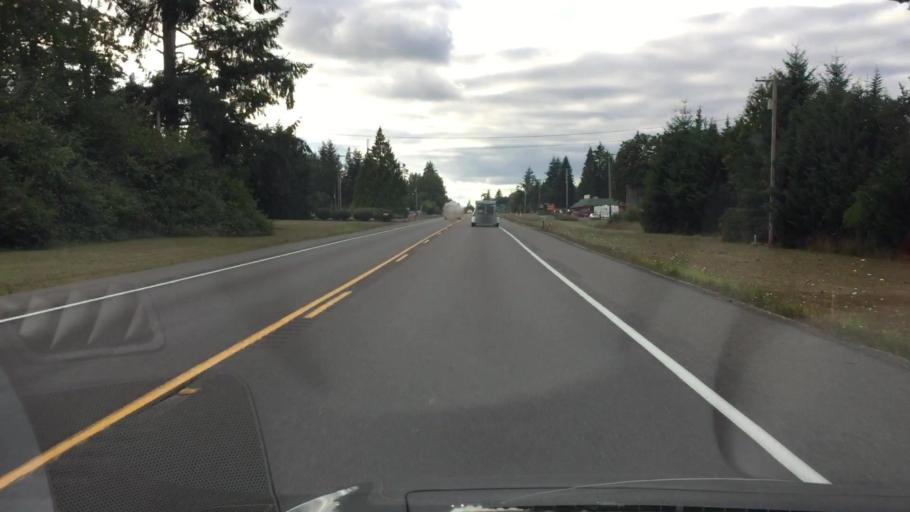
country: US
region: Washington
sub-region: Lewis County
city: Morton
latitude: 46.5207
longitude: -122.5862
